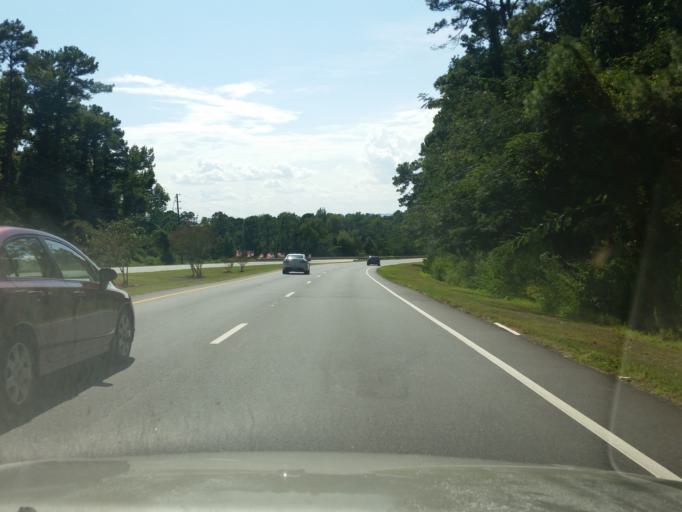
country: US
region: Alabama
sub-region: Baldwin County
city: Spanish Fort
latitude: 30.6674
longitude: -87.9146
